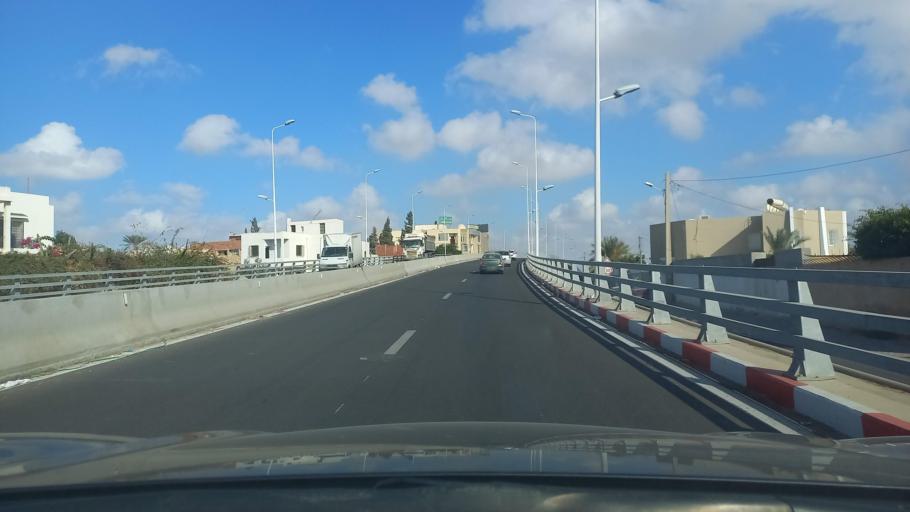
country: TN
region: Safaqis
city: Sfax
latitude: 34.7444
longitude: 10.7252
